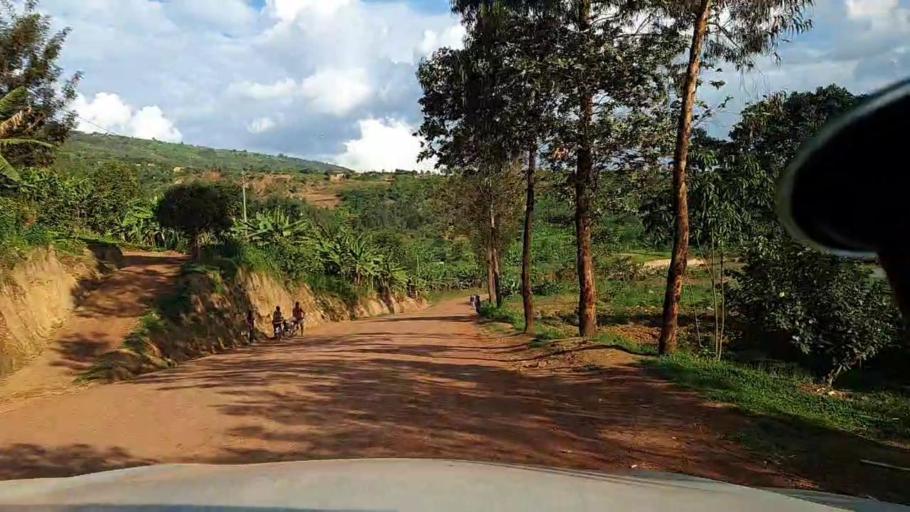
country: RW
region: Kigali
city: Kigali
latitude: -1.9304
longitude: 29.9941
